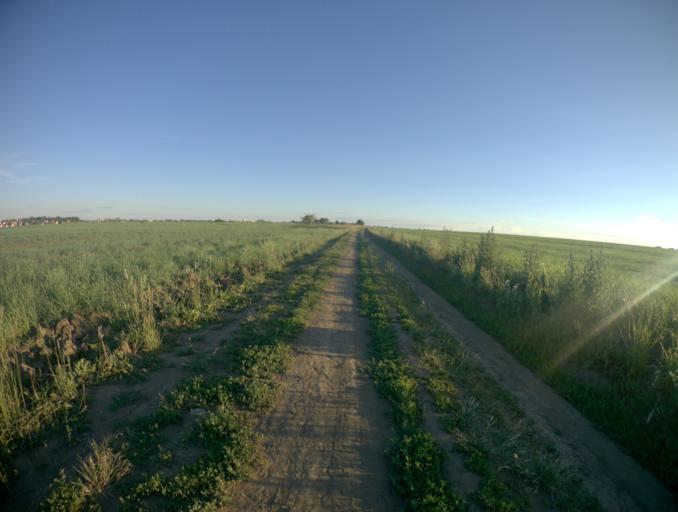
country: RU
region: Vladimir
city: Bogolyubovo
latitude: 56.2034
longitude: 40.5057
